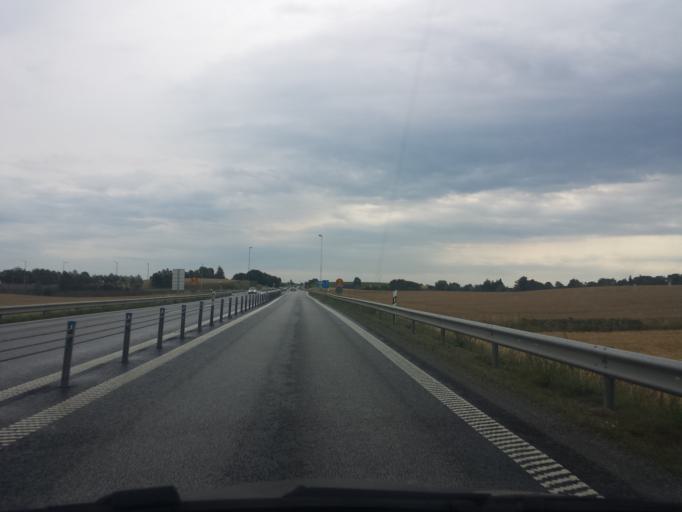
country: SE
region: Skane
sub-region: Skurups Kommun
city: Rydsgard
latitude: 55.4830
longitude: 13.5885
